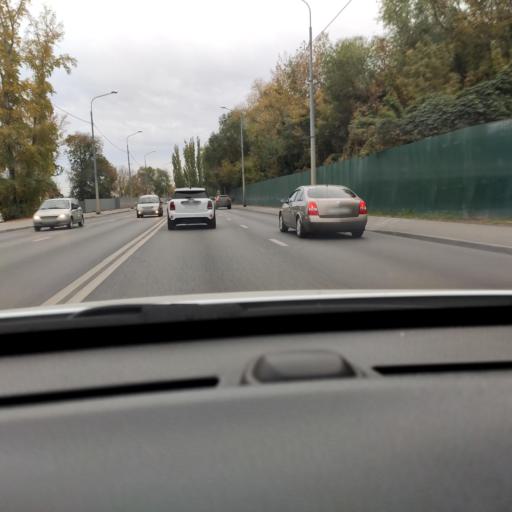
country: RU
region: Voronezj
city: Voronezh
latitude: 51.6891
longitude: 39.2317
